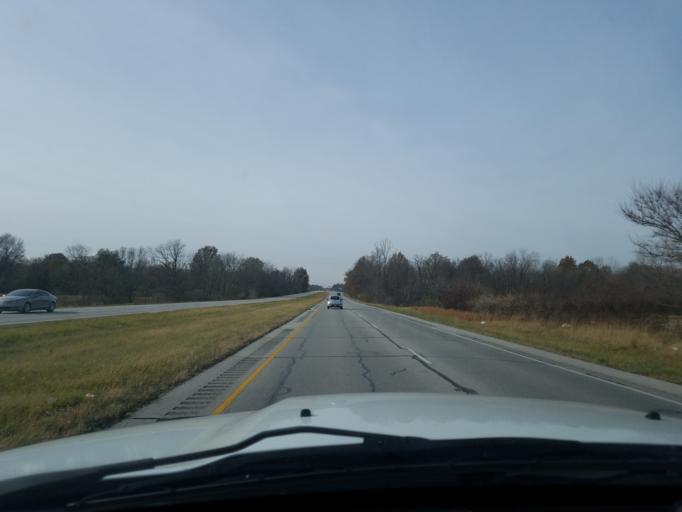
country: US
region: Indiana
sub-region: Delaware County
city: Yorktown
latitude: 40.2194
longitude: -85.4735
